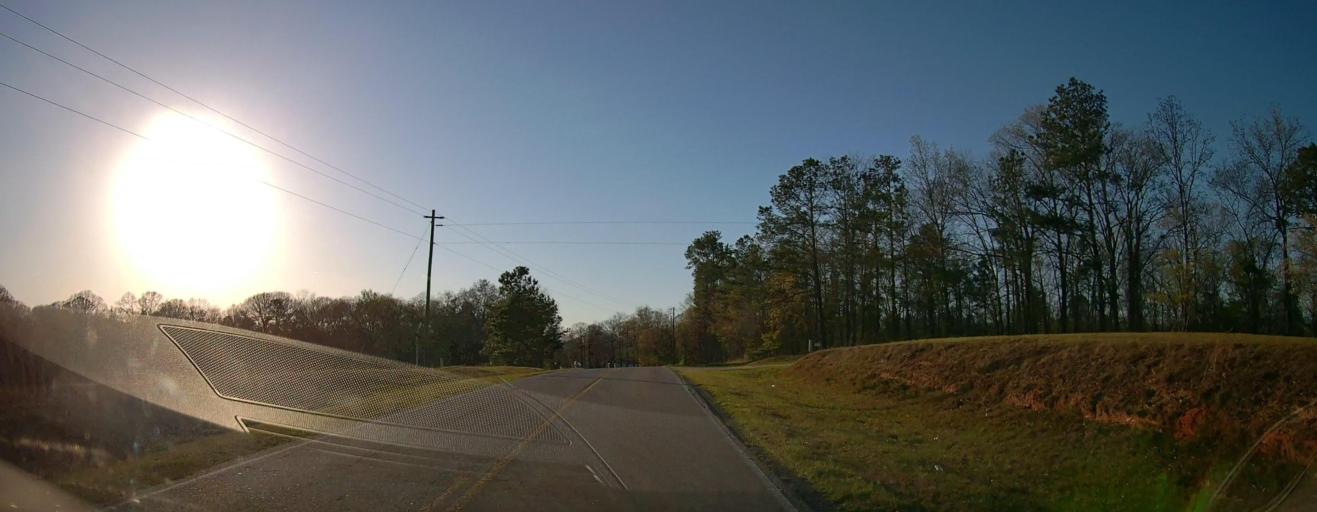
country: US
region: Georgia
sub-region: Wilkinson County
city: Gordon
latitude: 32.8815
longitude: -83.2794
